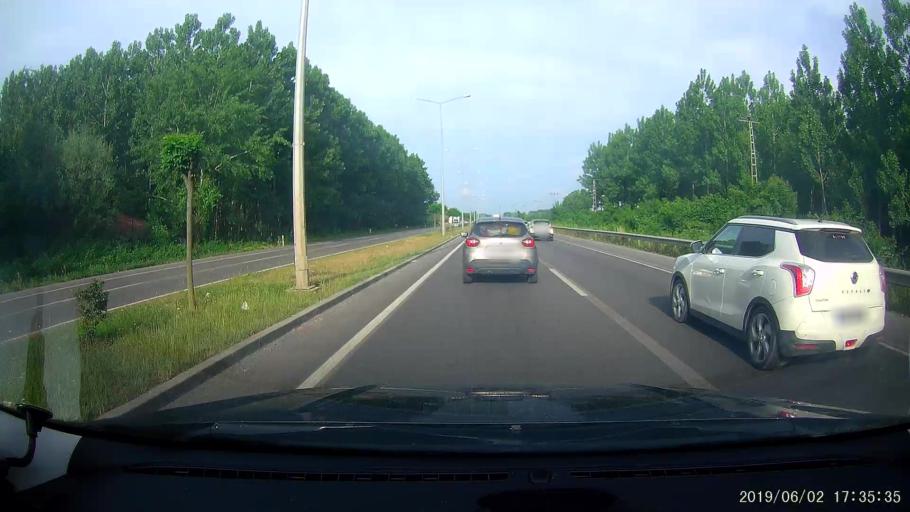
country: TR
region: Samsun
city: Terme
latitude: 41.2195
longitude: 36.8854
